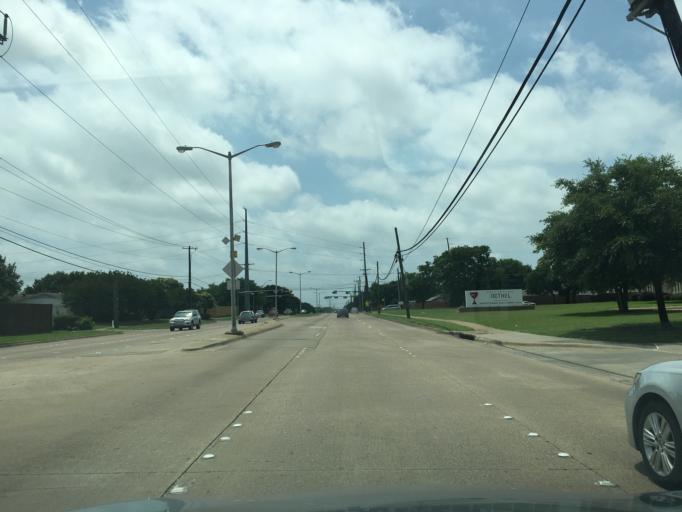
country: US
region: Texas
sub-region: Dallas County
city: Garland
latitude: 32.9253
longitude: -96.6831
